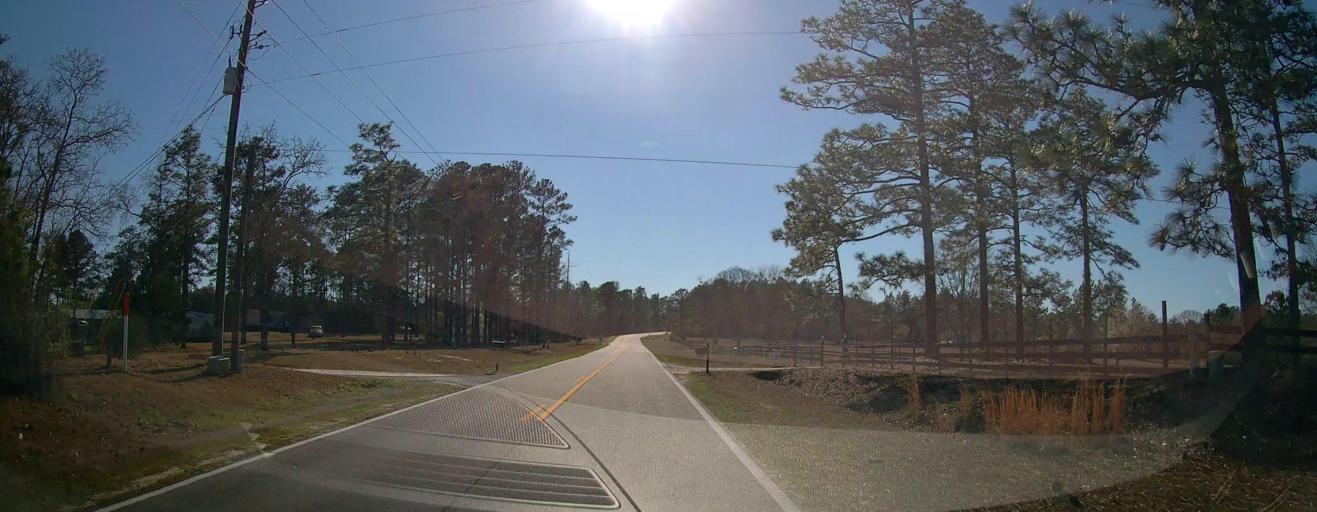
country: US
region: Georgia
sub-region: Peach County
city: Byron
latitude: 32.6941
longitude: -83.7810
